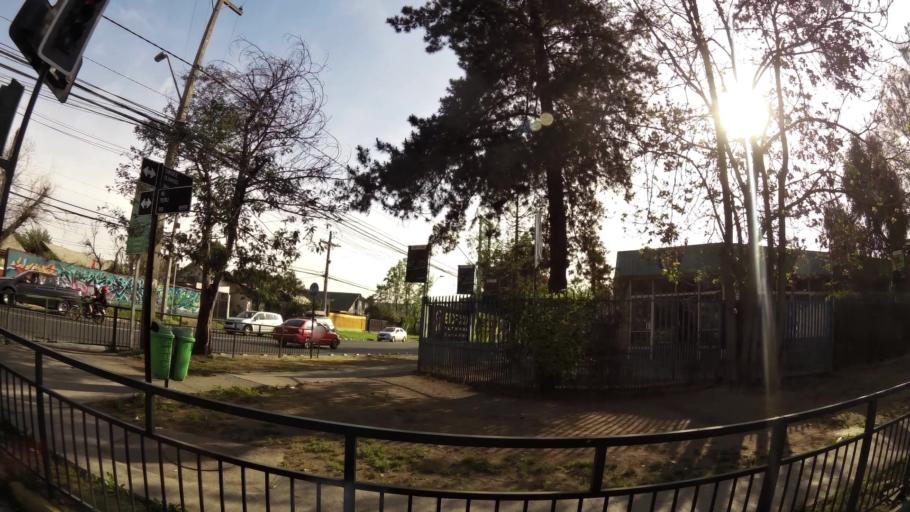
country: CL
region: Santiago Metropolitan
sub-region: Provincia de Santiago
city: La Pintana
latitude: -33.5396
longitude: -70.5858
